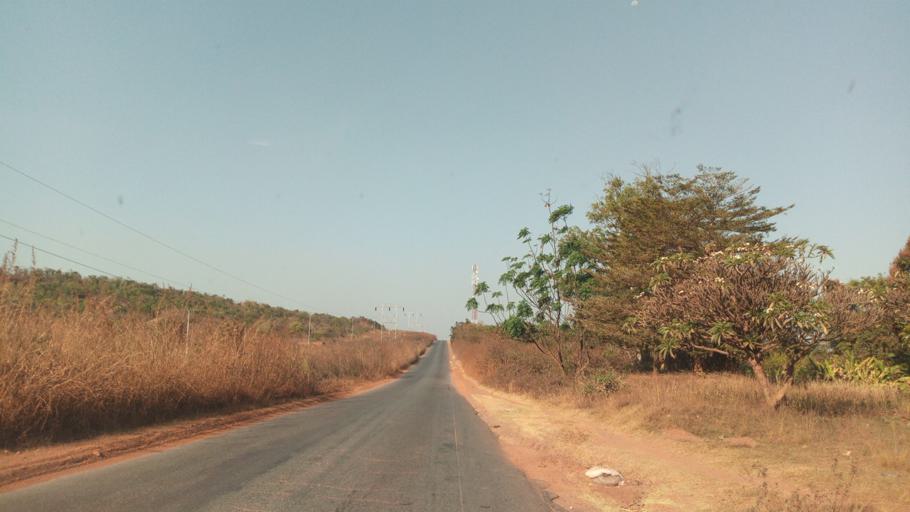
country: CD
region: Katanga
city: Likasi
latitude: -11.0003
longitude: 26.8858
